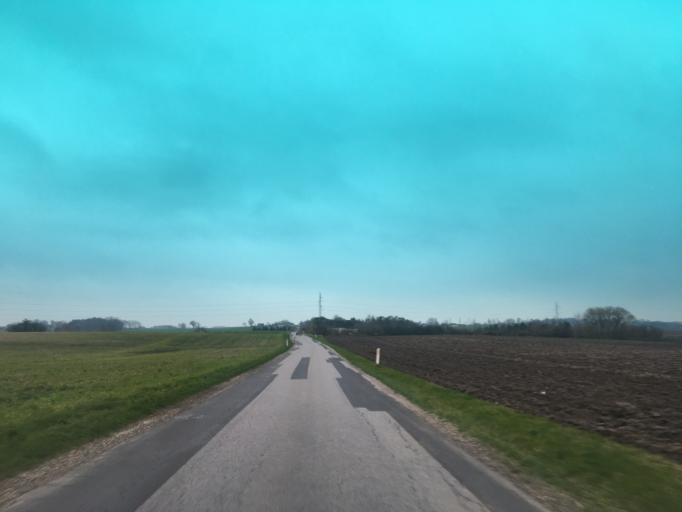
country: DK
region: Zealand
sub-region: Slagelse Kommune
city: Skaelskor
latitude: 55.2357
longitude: 11.4236
